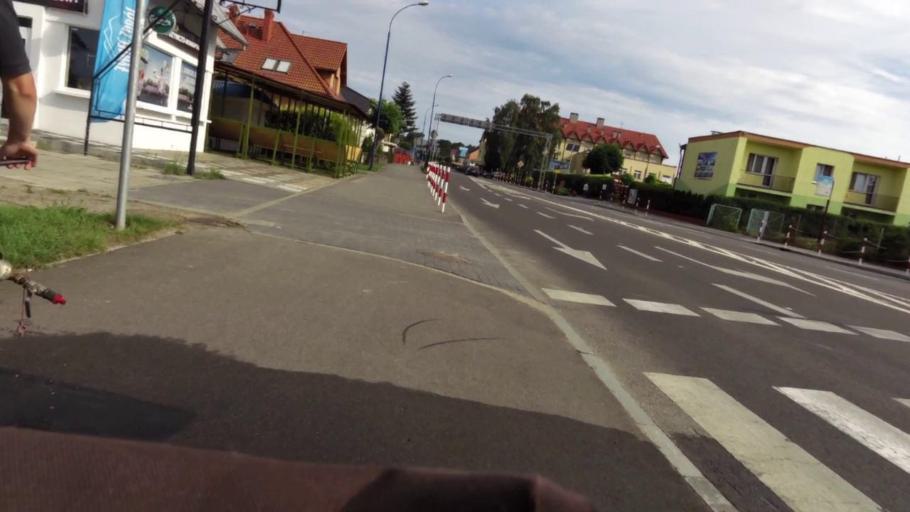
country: PL
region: West Pomeranian Voivodeship
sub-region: Powiat kamienski
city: Dziwnow
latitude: 54.0327
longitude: 14.8070
